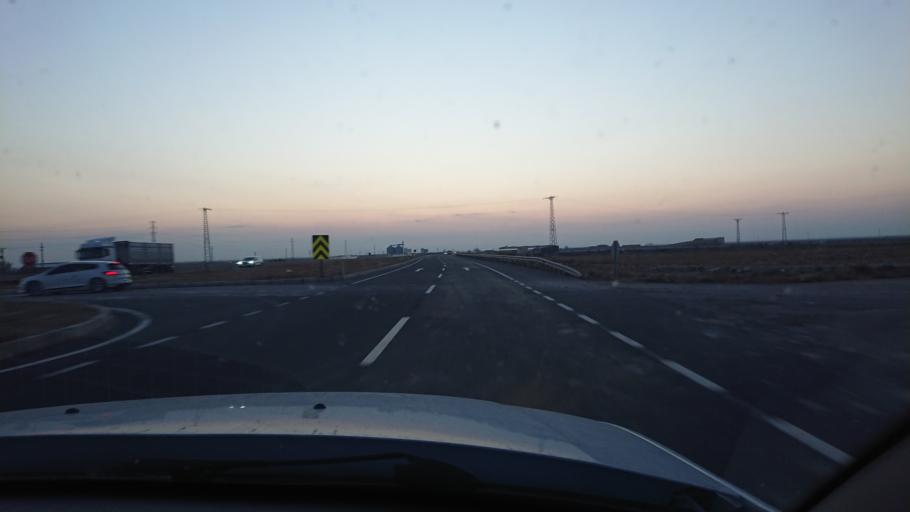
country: TR
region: Aksaray
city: Yesilova
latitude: 38.3107
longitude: 33.8322
